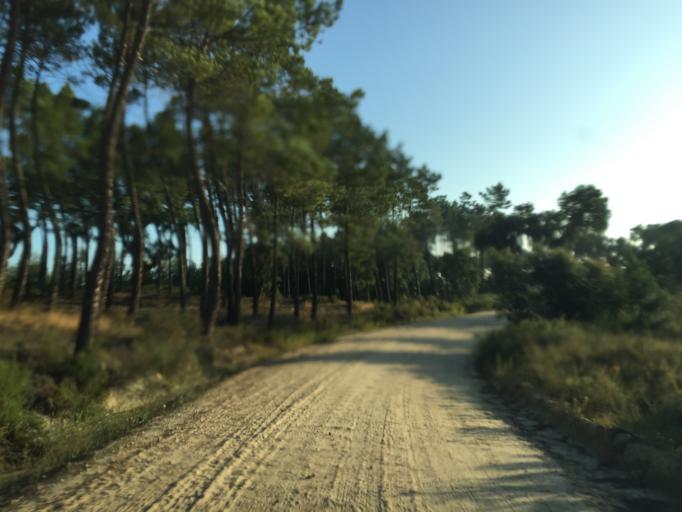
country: PT
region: Portalegre
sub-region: Ponte de Sor
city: Santo Andre
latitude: 39.1010
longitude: -8.3434
